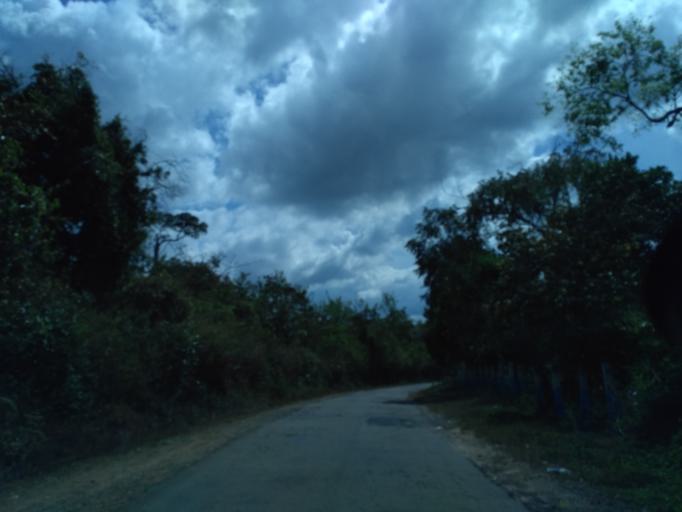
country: IN
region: Karnataka
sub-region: Kodagu
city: Madikeri
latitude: 12.4090
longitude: 75.7131
